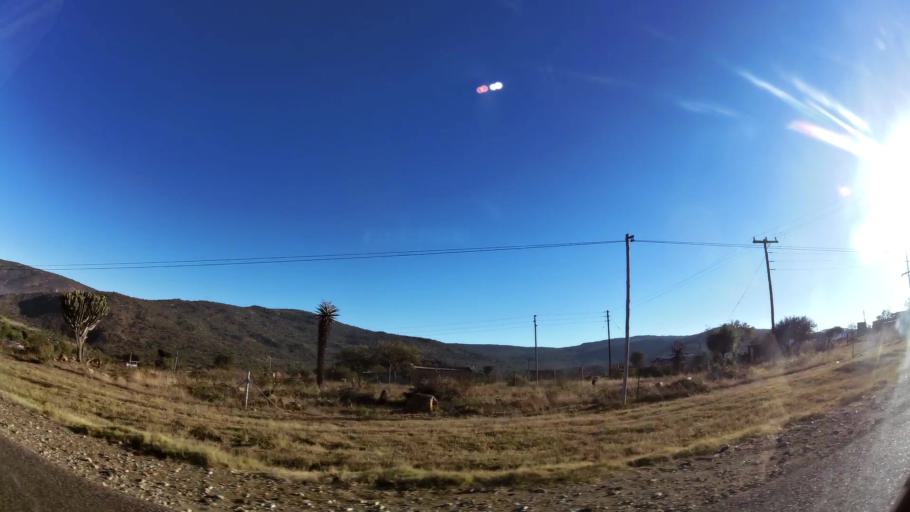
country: ZA
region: Limpopo
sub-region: Capricorn District Municipality
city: Mankoeng
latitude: -23.9302
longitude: 29.8545
